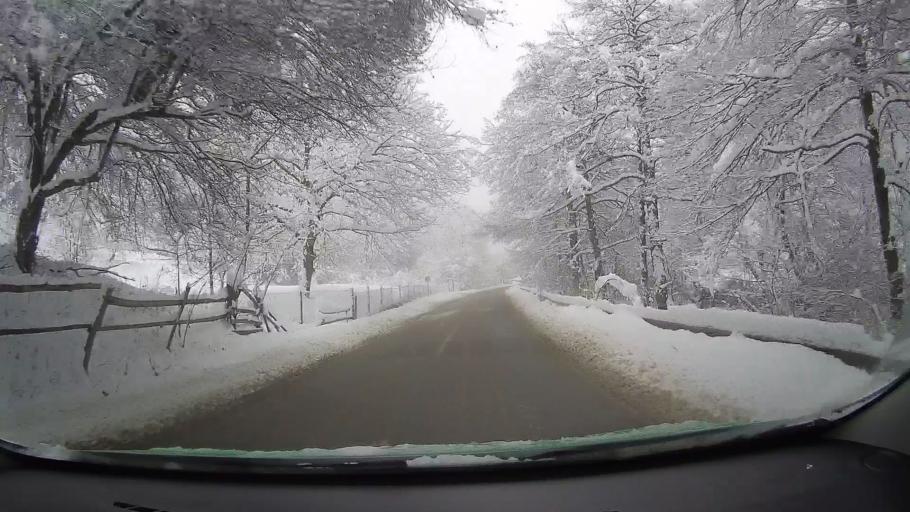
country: RO
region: Sibiu
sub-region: Comuna Tilisca
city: Tilisca
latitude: 45.8029
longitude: 23.8332
